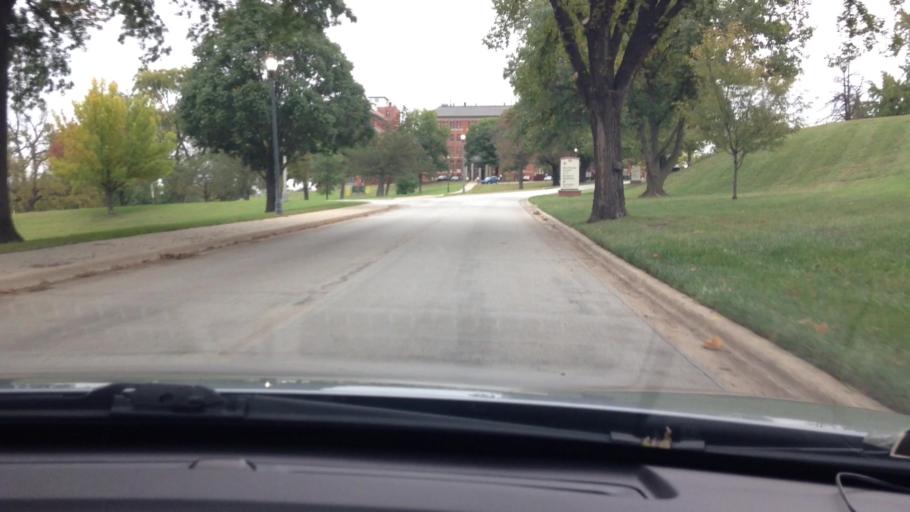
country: US
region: Kansas
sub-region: Leavenworth County
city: Lansing
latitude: 39.2796
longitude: -94.8976
